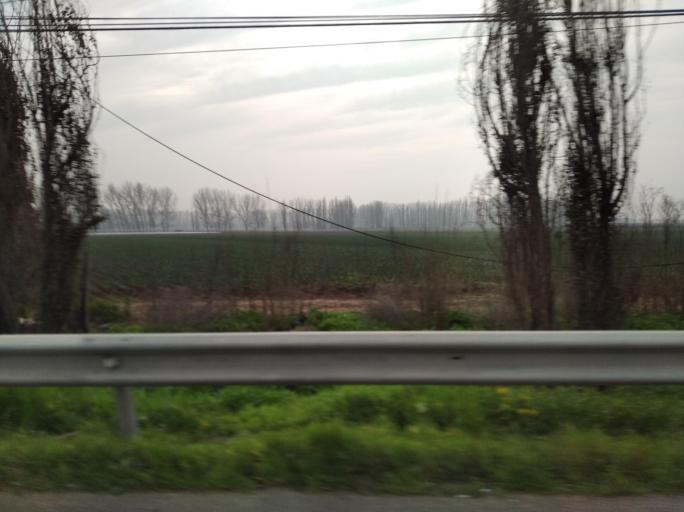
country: CL
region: Santiago Metropolitan
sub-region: Provincia de Chacabuco
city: Lampa
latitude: -33.3199
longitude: -70.8309
